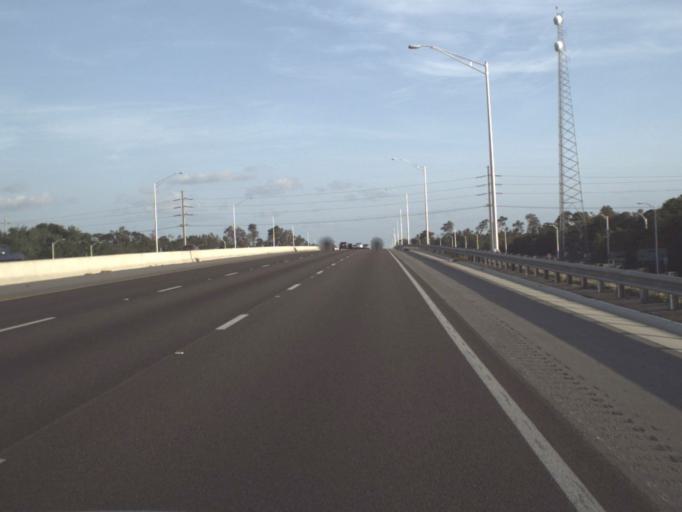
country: US
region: Florida
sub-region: Brevard County
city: Mims
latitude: 28.6685
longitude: -80.8708
